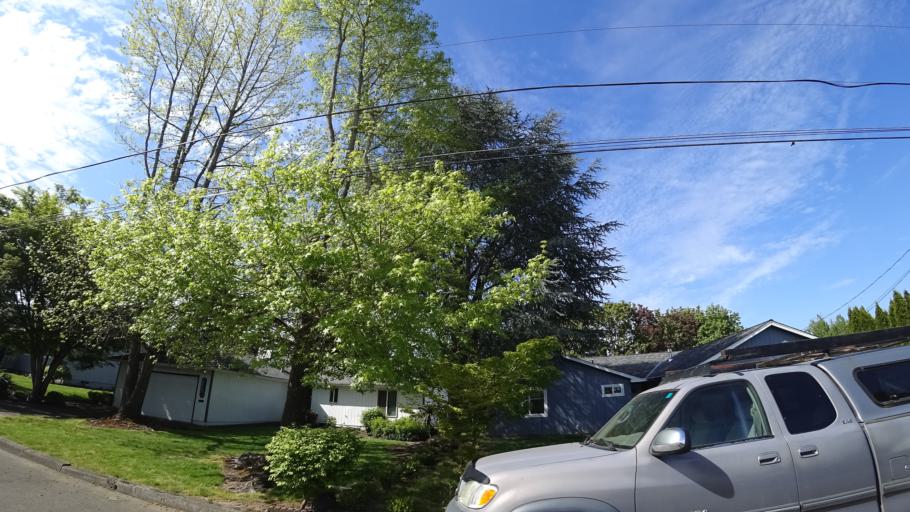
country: US
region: Oregon
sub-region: Washington County
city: Aloha
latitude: 45.4997
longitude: -122.8890
